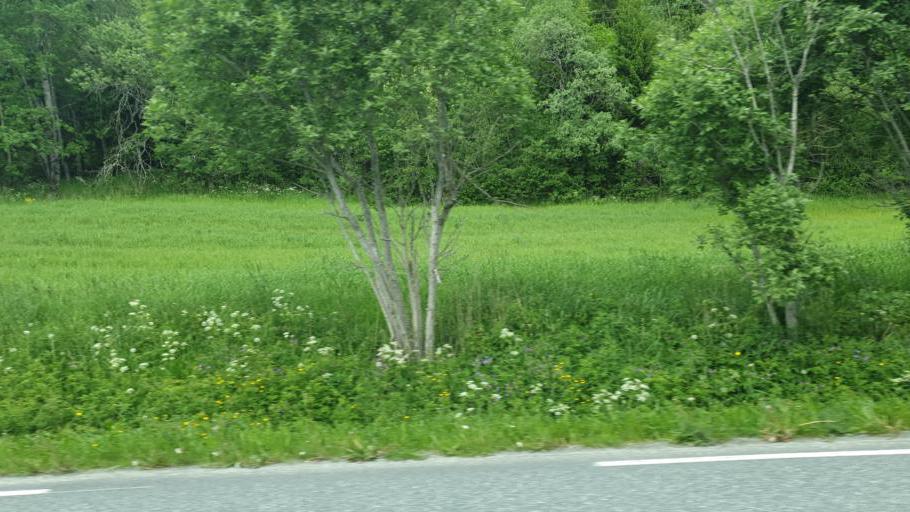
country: NO
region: Sor-Trondelag
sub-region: Trondheim
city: Trondheim
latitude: 63.5595
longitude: 10.3149
